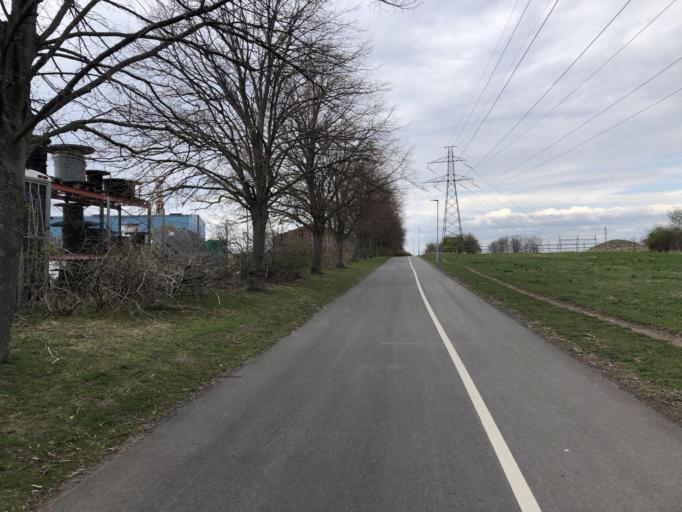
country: SE
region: Skane
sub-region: Malmo
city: Tygelsjo
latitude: 55.5576
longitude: 13.0418
